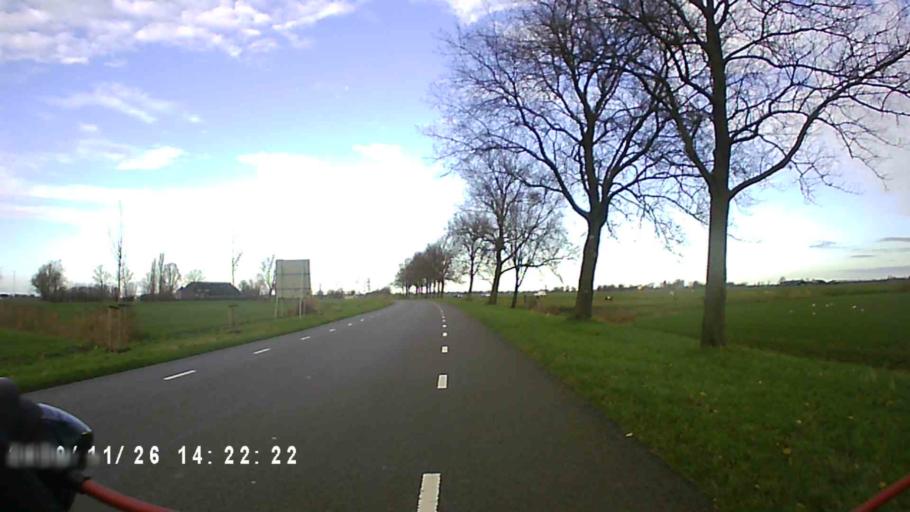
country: NL
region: Groningen
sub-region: Gemeente Appingedam
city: Appingedam
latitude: 53.3305
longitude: 6.8670
